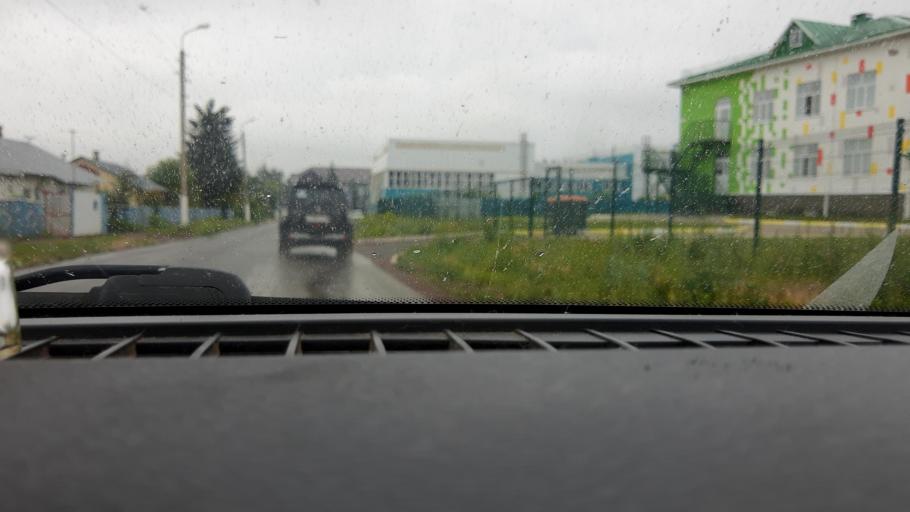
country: RU
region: Bashkortostan
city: Belebey
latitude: 54.1118
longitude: 54.1038
